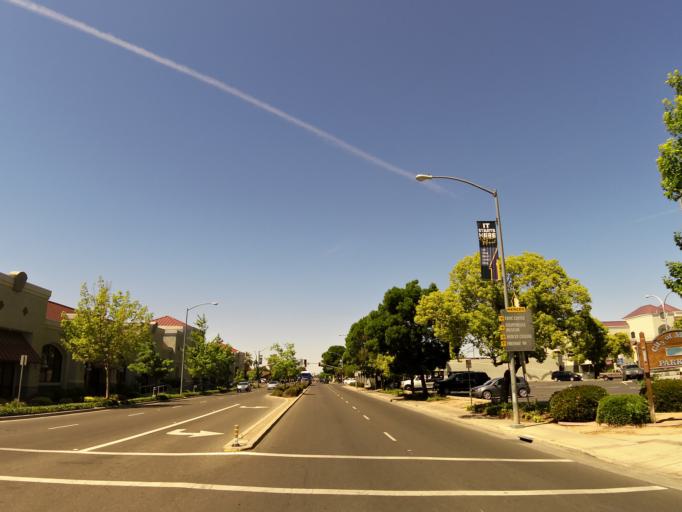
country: US
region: California
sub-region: Merced County
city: Merced
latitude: 37.3005
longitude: -120.4839
